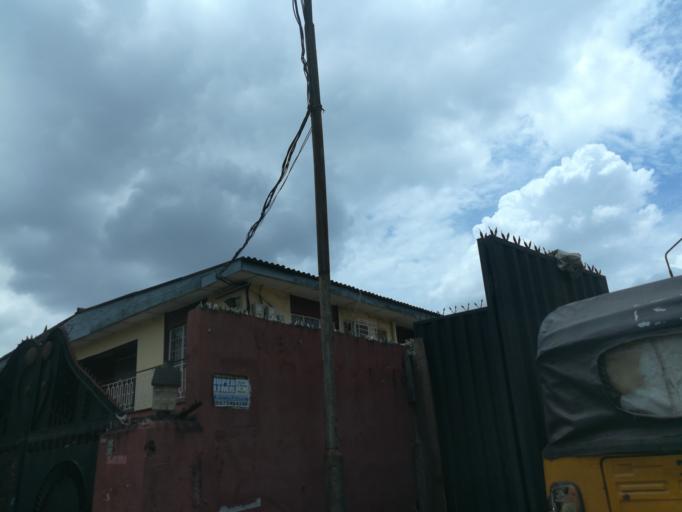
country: NG
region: Lagos
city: Ikeja
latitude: 6.6056
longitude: 3.3489
